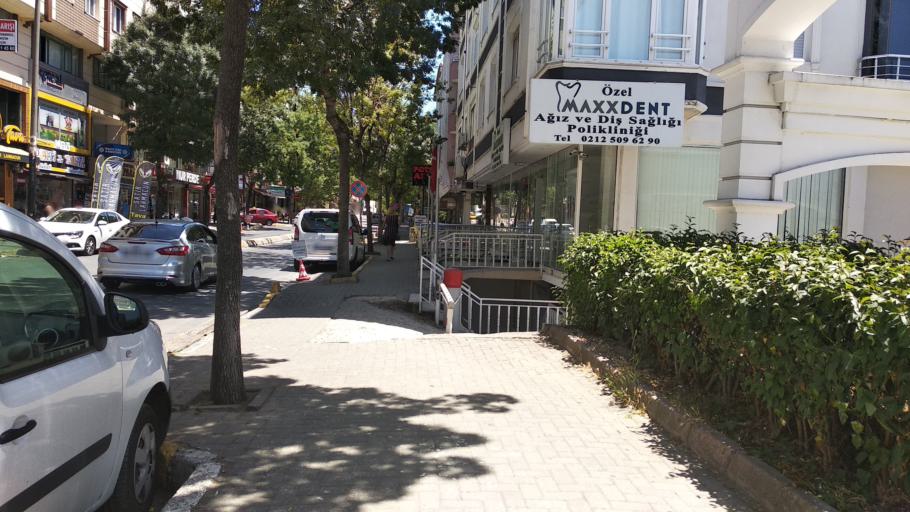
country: TR
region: Istanbul
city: Yakuplu
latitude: 40.9780
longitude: 28.7214
